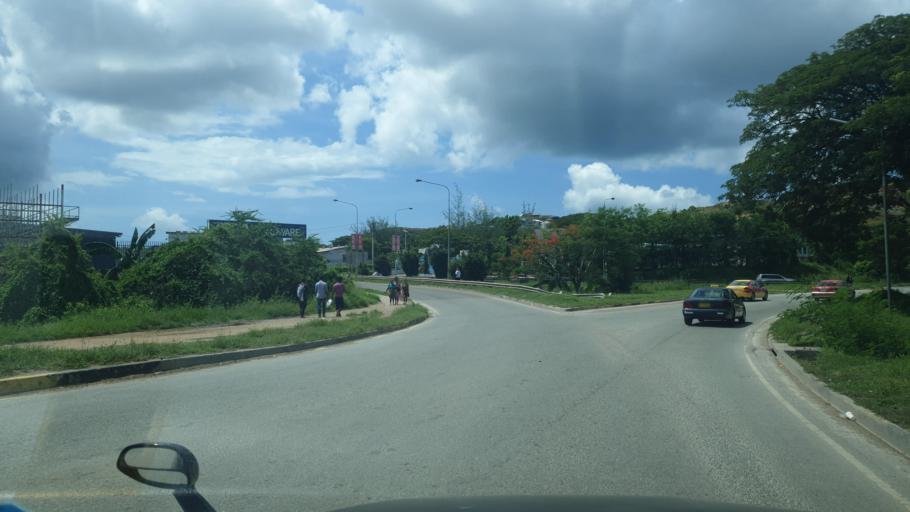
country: PG
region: National Capital
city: Port Moresby
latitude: -9.3976
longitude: 147.1600
